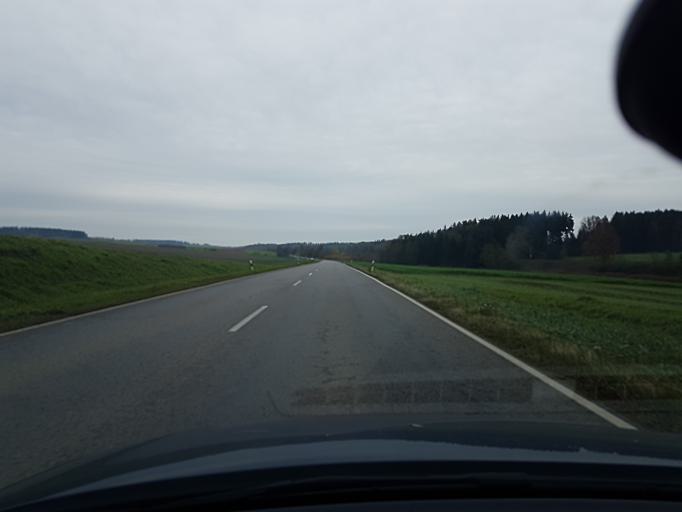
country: DE
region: Bavaria
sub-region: Upper Palatinate
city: Pfakofen
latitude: 48.8506
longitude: 12.1846
